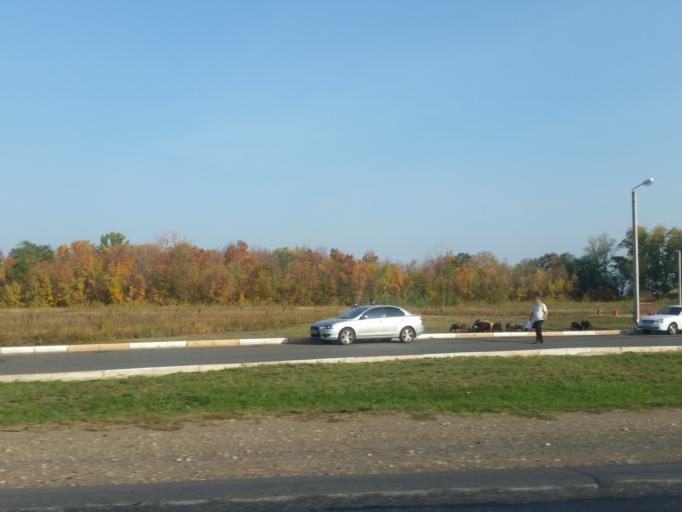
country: RU
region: Ulyanovsk
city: Mirnyy
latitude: 54.3723
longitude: 48.7376
